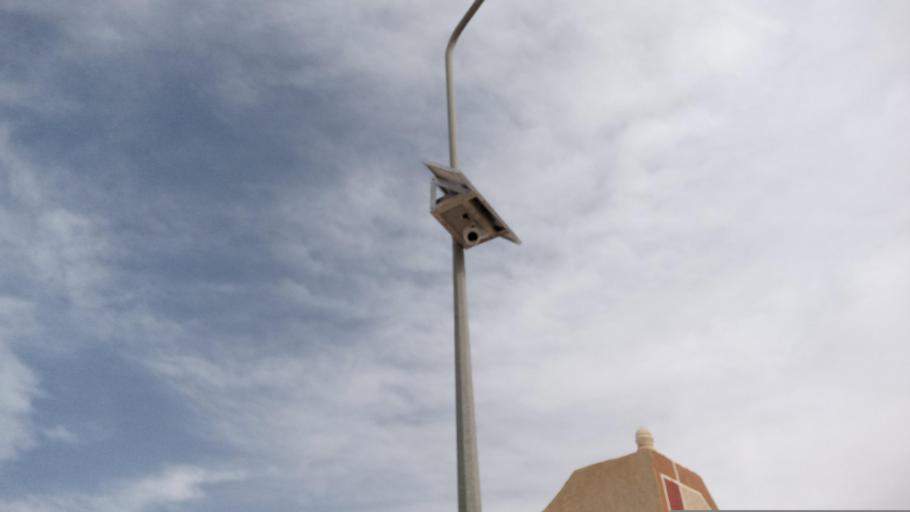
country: TN
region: Qibili
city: El Golaa
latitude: 33.4964
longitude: 8.8620
